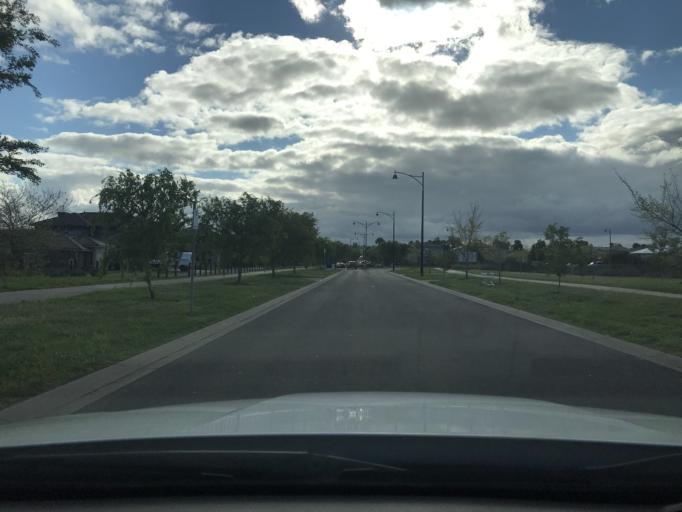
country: AU
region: Victoria
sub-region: Hume
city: Roxburgh Park
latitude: -37.5892
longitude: 144.9078
